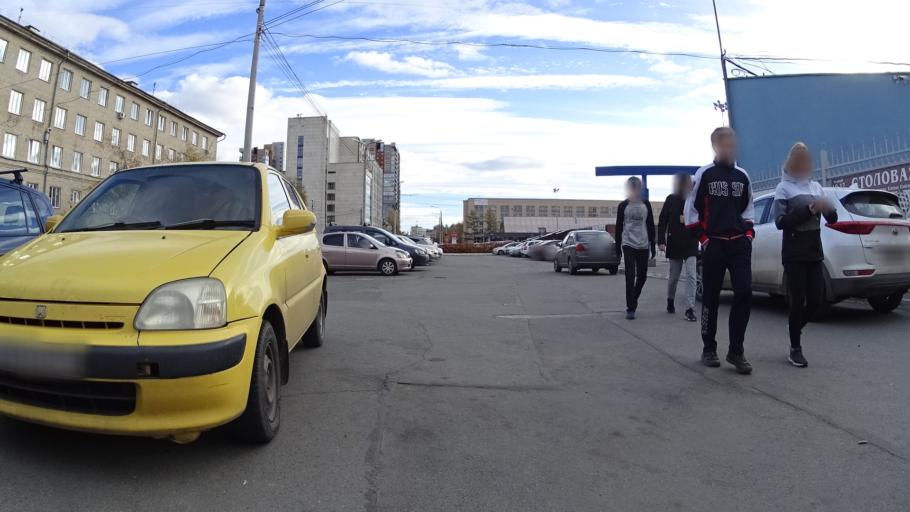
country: RU
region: Chelyabinsk
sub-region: Gorod Chelyabinsk
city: Chelyabinsk
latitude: 55.1606
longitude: 61.3644
